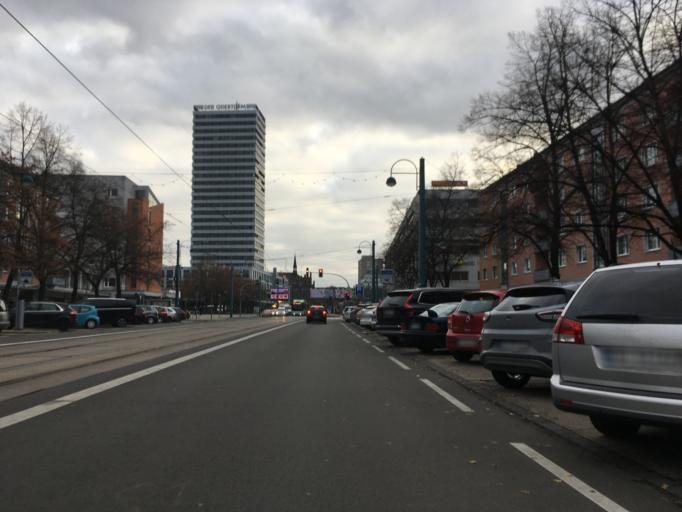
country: DE
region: Brandenburg
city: Frankfurt (Oder)
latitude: 52.3446
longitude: 14.5510
